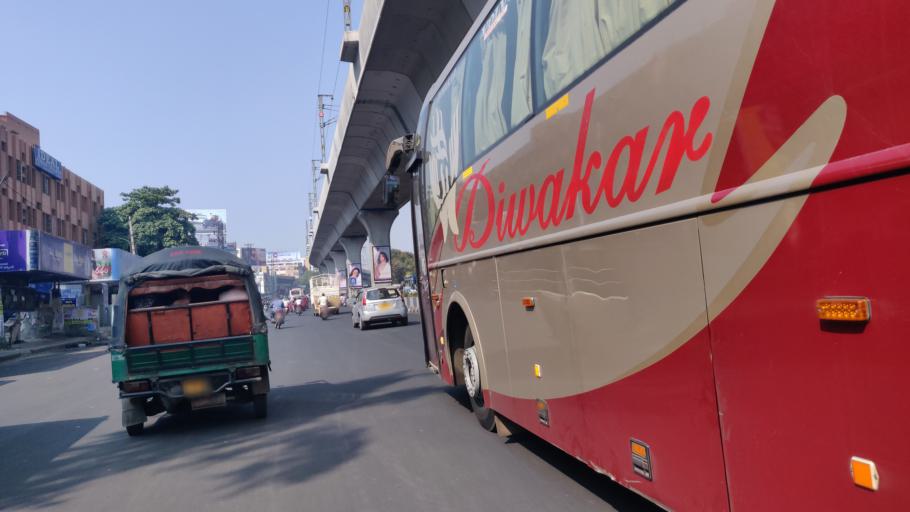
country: IN
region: Telangana
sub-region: Rangareddi
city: Gaddi Annaram
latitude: 17.3685
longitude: 78.5222
